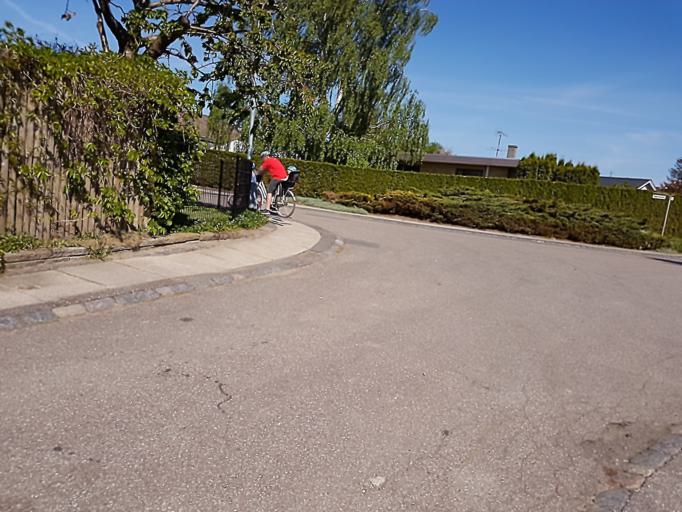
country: DK
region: Capital Region
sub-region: Egedal Kommune
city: Olstykke
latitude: 55.7936
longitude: 12.1365
